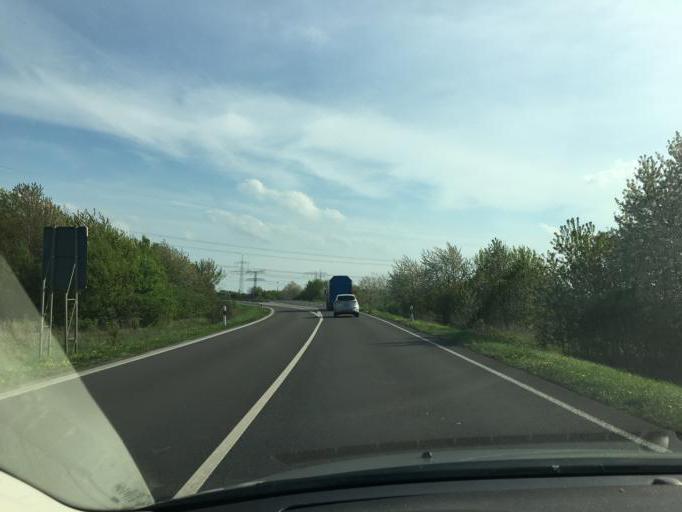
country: DE
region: Saxony-Anhalt
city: Dahlenwarsleben
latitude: 52.2058
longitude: 11.5460
